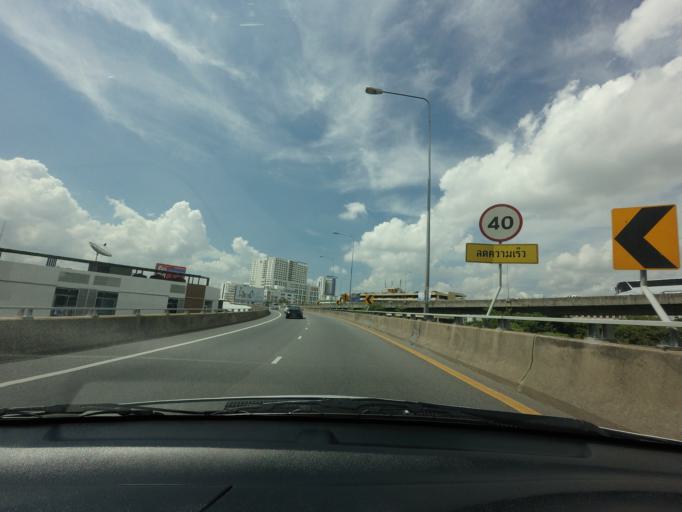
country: TH
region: Bangkok
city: Phaya Thai
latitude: 13.7723
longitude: 100.5325
